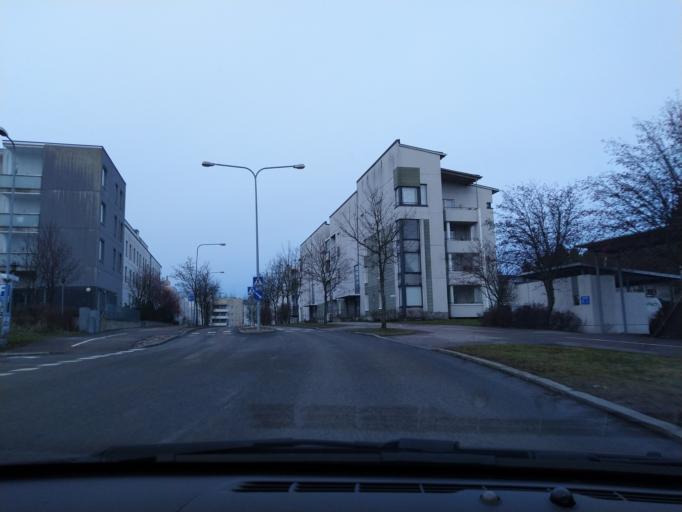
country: FI
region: Uusimaa
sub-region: Helsinki
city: Vantaa
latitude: 60.2373
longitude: 25.0677
